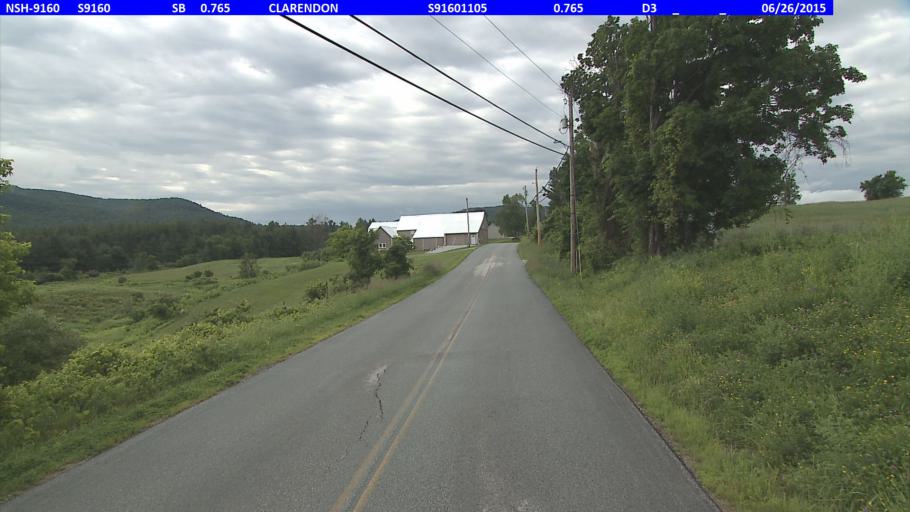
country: US
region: Vermont
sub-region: Rutland County
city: Rutland
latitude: 43.5384
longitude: -72.9480
